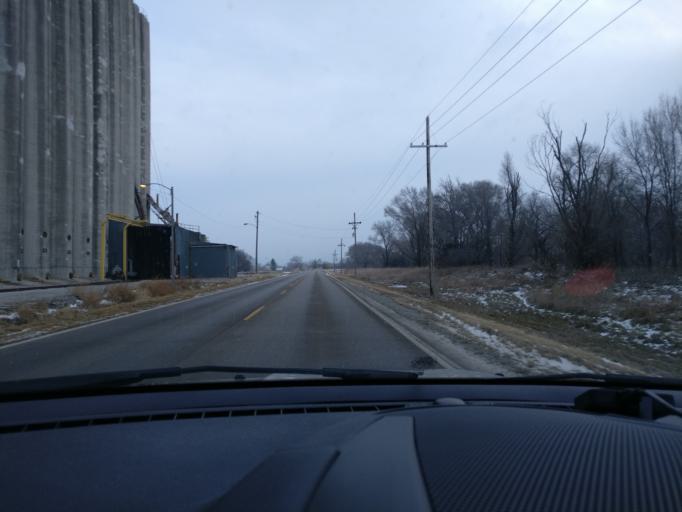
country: US
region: Nebraska
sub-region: Dodge County
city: Fremont
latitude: 41.4475
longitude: -96.5550
